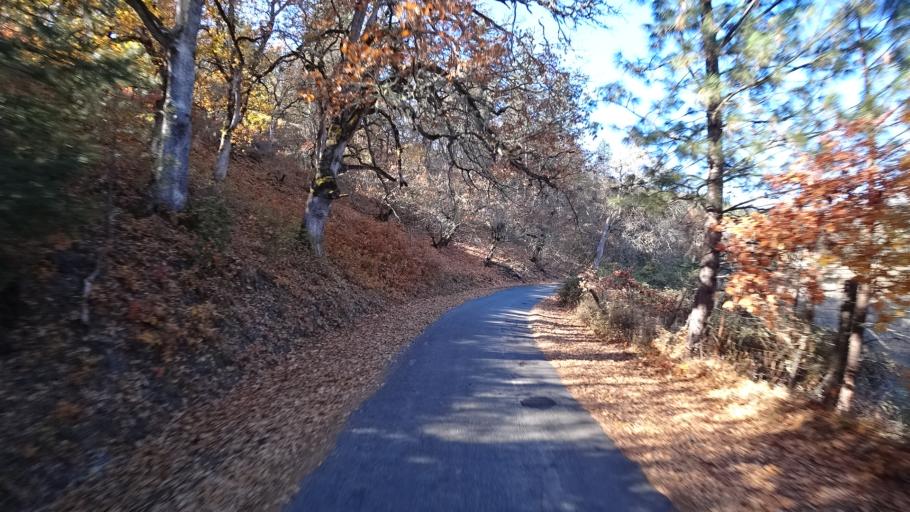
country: US
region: California
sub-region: Siskiyou County
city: Yreka
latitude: 41.8409
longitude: -122.8901
